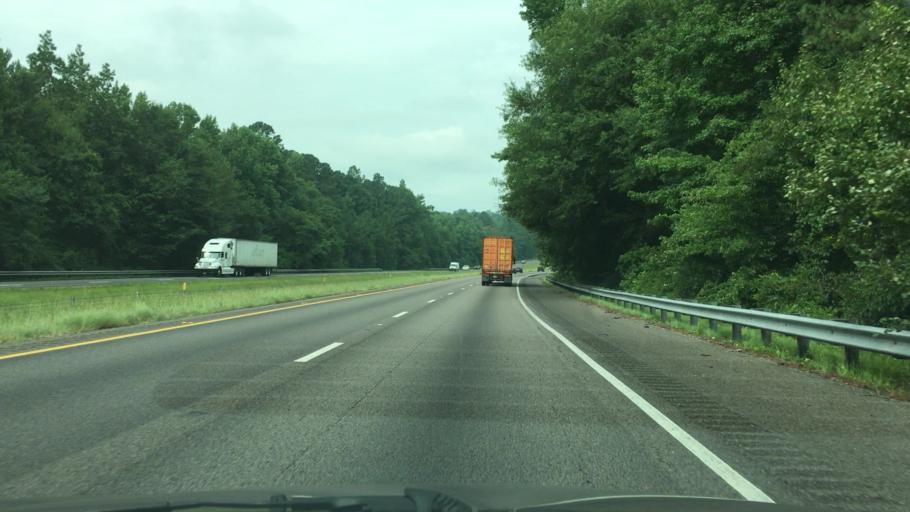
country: US
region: South Carolina
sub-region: Edgefield County
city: Murphys Estates
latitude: 33.5728
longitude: -81.9109
